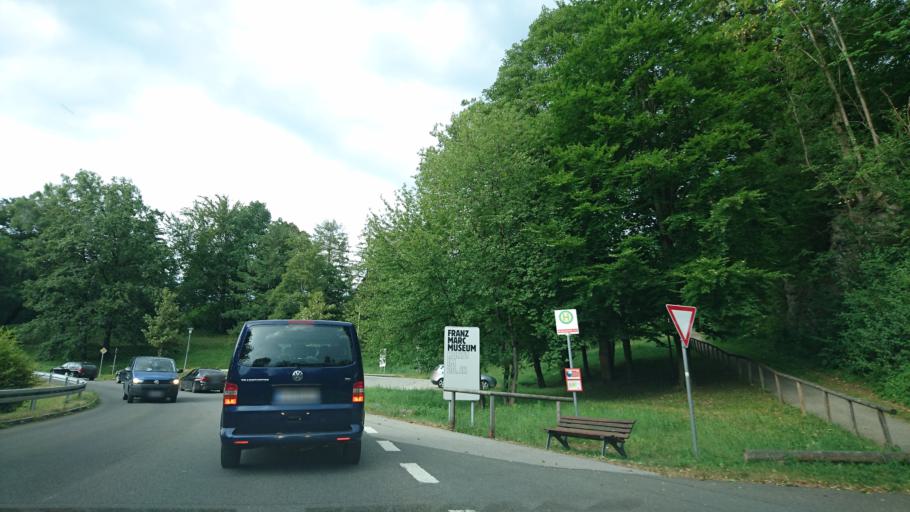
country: DE
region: Bavaria
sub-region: Upper Bavaria
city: Kochel
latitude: 47.6495
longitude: 11.3625
